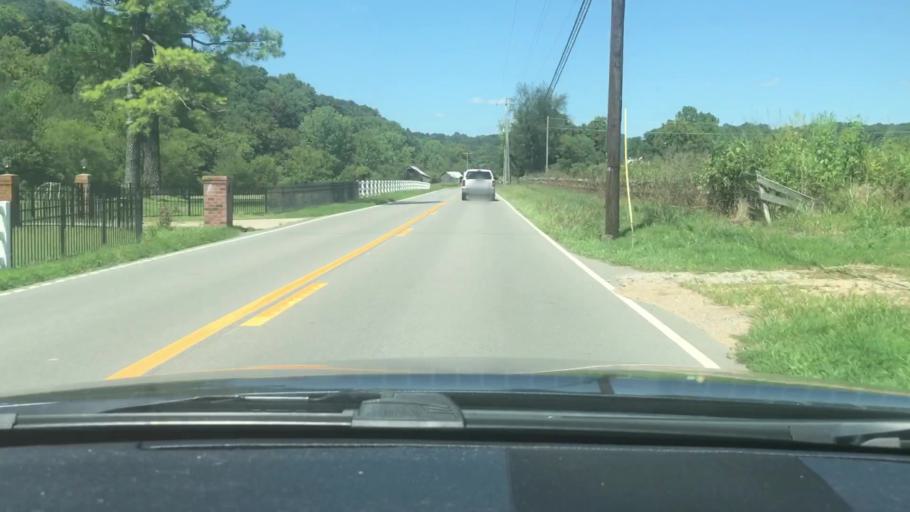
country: US
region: Tennessee
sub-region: Sumner County
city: White House
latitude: 36.4622
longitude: -86.5567
